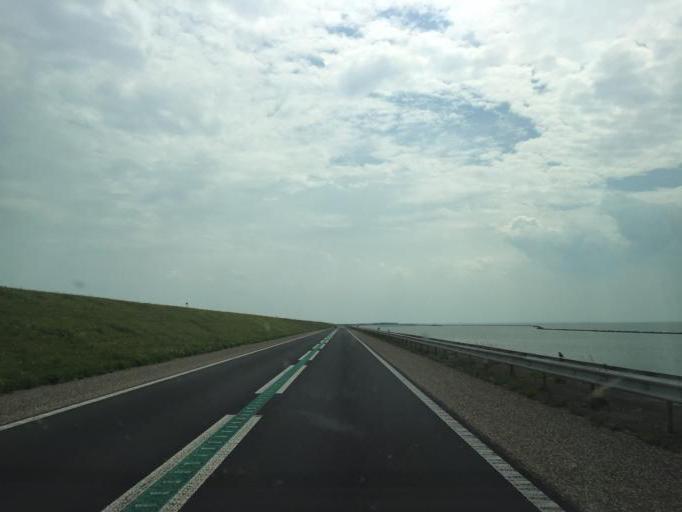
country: NL
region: North Holland
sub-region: Gemeente Enkhuizen
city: Enkhuizen
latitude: 52.6626
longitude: 5.3785
